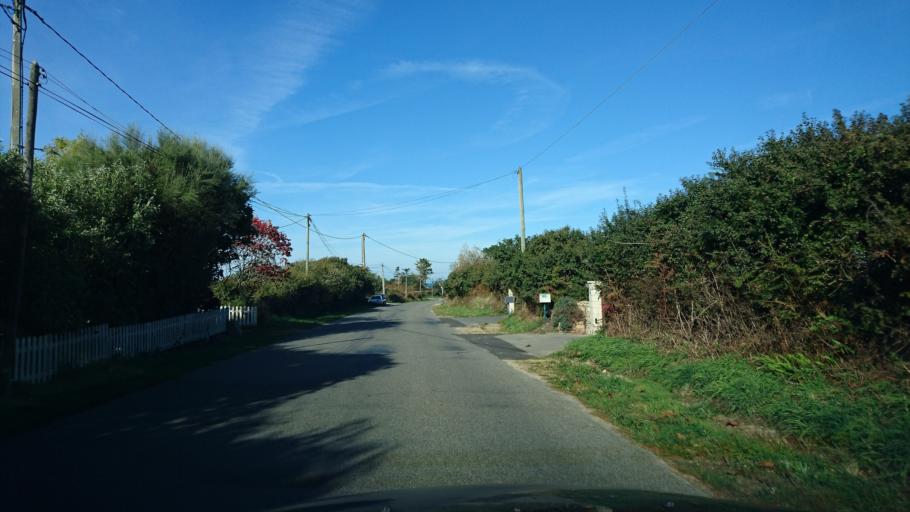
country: FR
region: Brittany
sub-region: Departement du Finistere
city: Lampaul-Plouarzel
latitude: 48.4328
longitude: -4.7702
